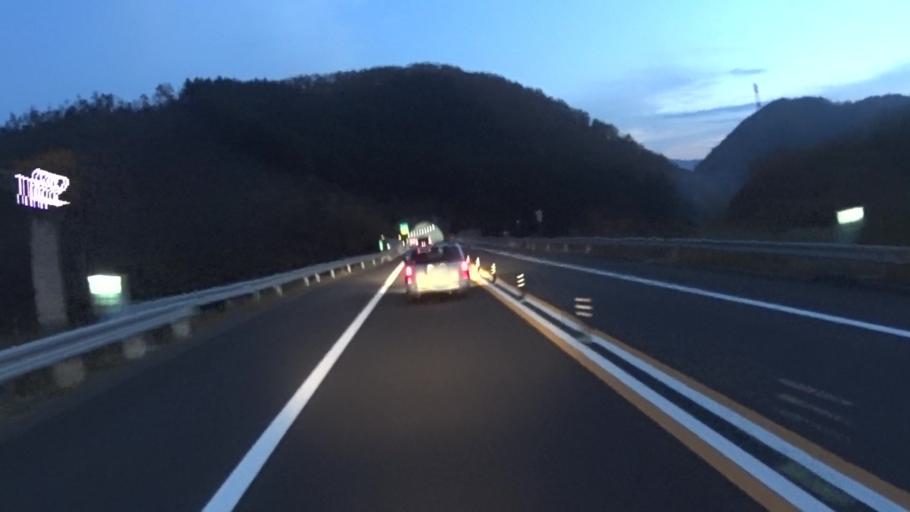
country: JP
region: Kyoto
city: Ayabe
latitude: 35.3198
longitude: 135.3176
